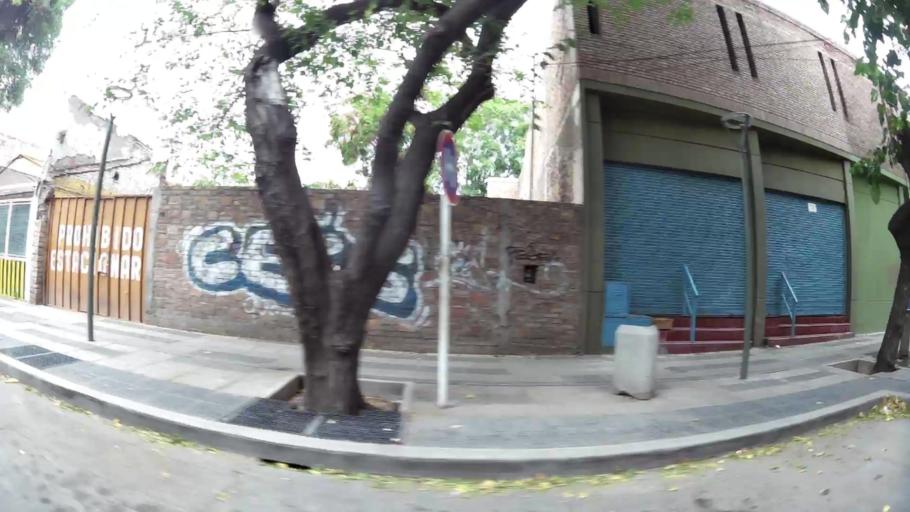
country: AR
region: Mendoza
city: Mendoza
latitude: -32.8824
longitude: -68.8366
